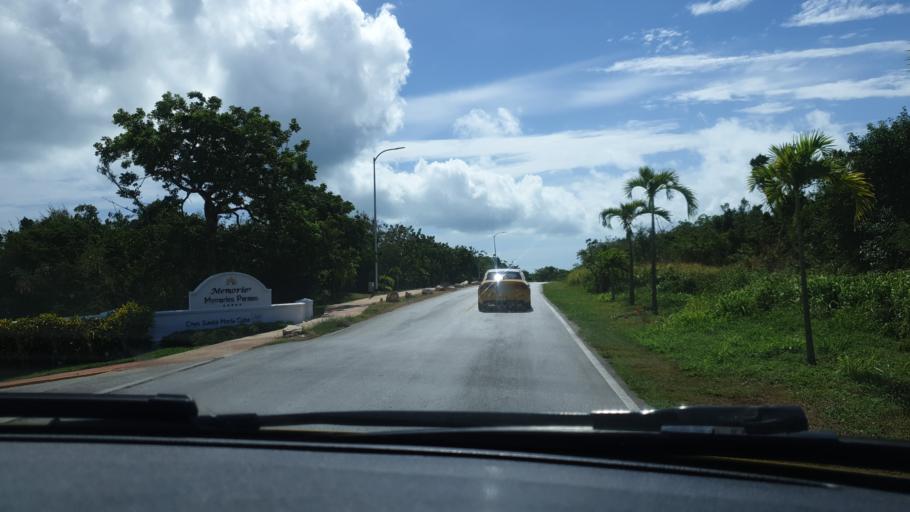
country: CU
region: Sancti Spiritus
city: Yaguajay
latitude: 22.6559
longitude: -79.0312
